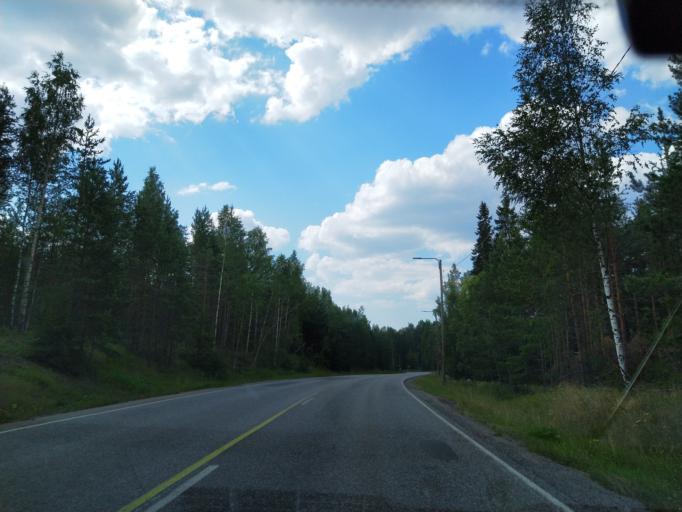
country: FI
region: Uusimaa
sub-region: Helsinki
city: Kirkkonummi
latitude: 60.1081
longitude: 24.4823
